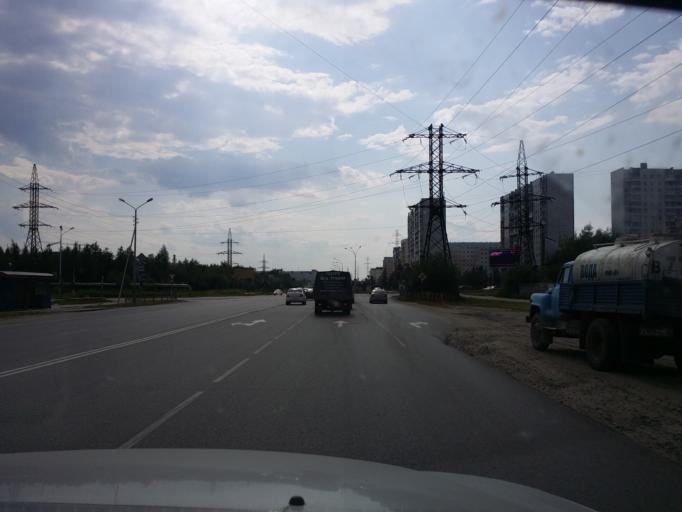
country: RU
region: Khanty-Mansiyskiy Avtonomnyy Okrug
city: Nizhnevartovsk
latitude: 60.9551
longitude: 76.5780
